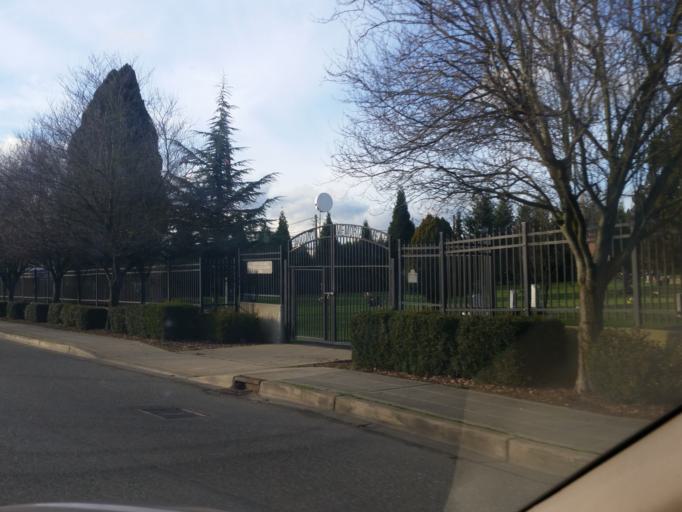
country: US
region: Washington
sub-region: King County
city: Woodinville
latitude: 47.7545
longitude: -122.1635
